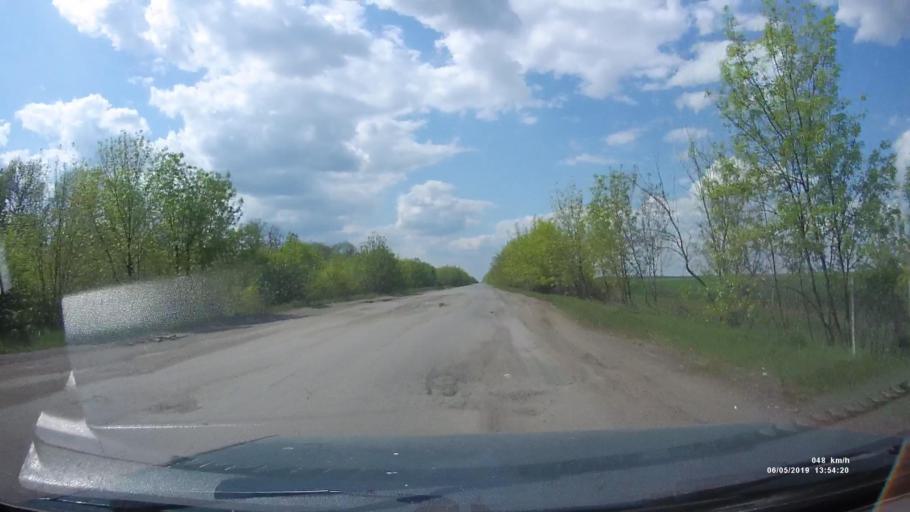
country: RU
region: Rostov
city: Melikhovskaya
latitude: 47.6738
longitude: 40.4489
